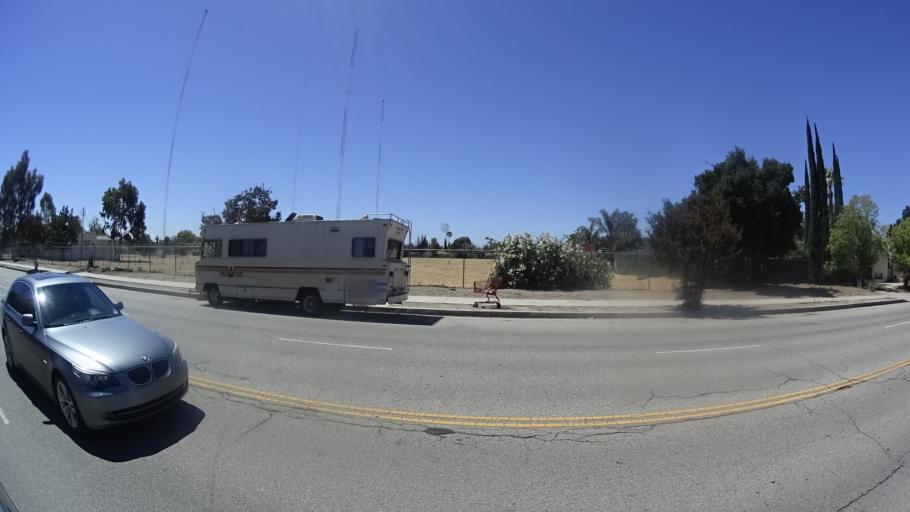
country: US
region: California
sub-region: Los Angeles County
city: San Fernando
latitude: 34.2500
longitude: -118.4551
